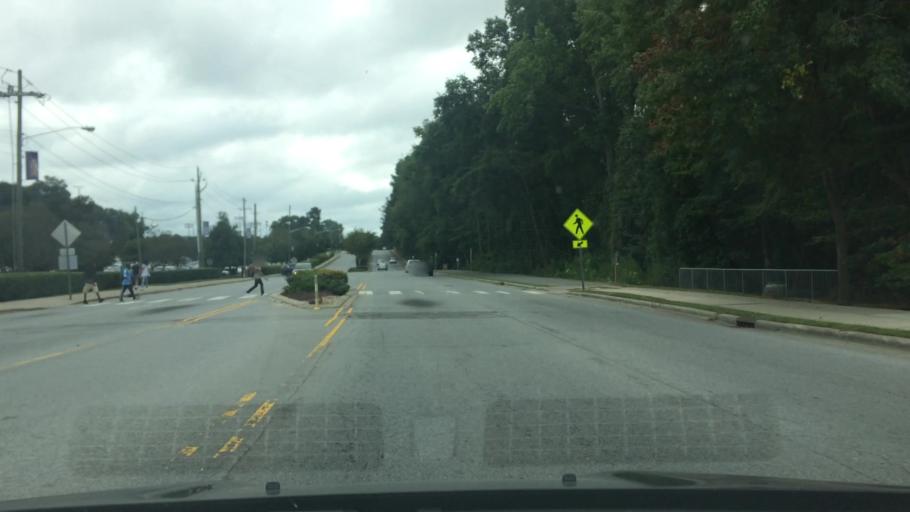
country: US
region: North Carolina
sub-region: Pitt County
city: Greenville
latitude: 35.5996
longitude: -77.3706
